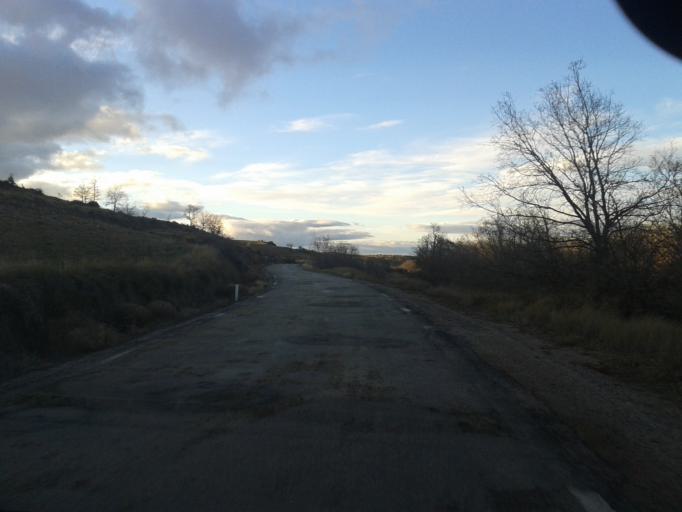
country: ES
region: Aragon
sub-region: Provincia de Teruel
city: Lagueruela
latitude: 41.0415
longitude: -1.2055
